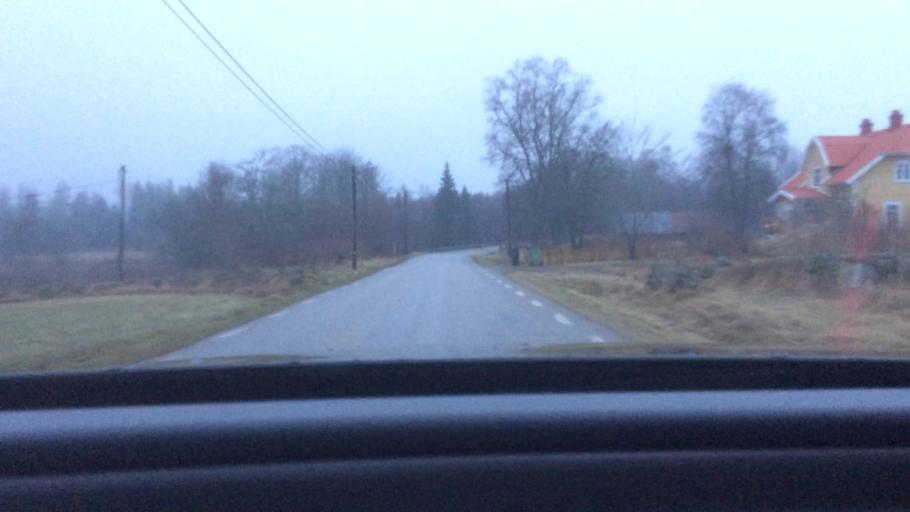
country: SE
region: Vaestra Goetaland
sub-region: Ulricehamns Kommun
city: Ulricehamn
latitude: 57.9538
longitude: 13.3876
